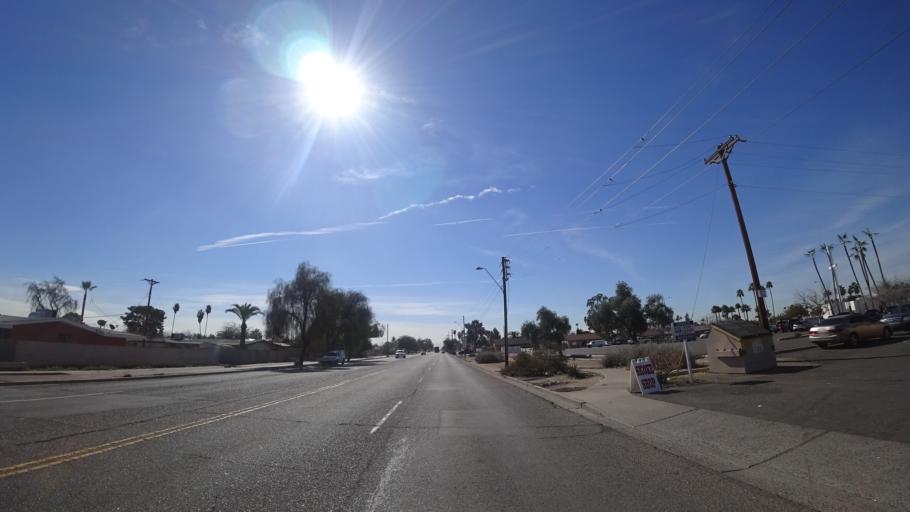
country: US
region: Arizona
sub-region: Maricopa County
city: Glendale
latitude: 33.5087
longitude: -112.1864
